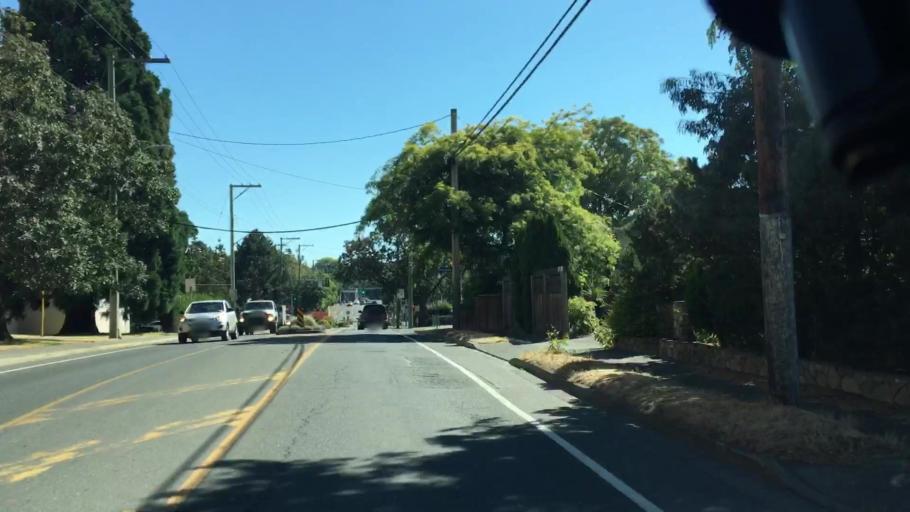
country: CA
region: British Columbia
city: Oak Bay
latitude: 48.4328
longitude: -123.3294
